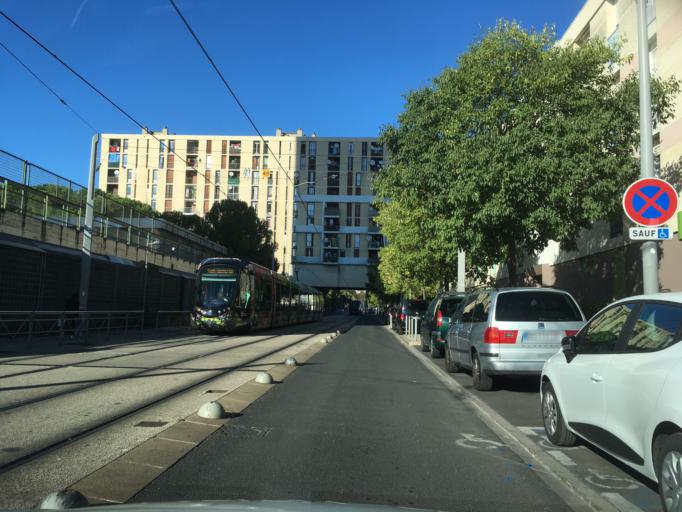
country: FR
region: Languedoc-Roussillon
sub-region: Departement de l'Herault
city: Juvignac
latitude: 43.6217
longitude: 3.8175
